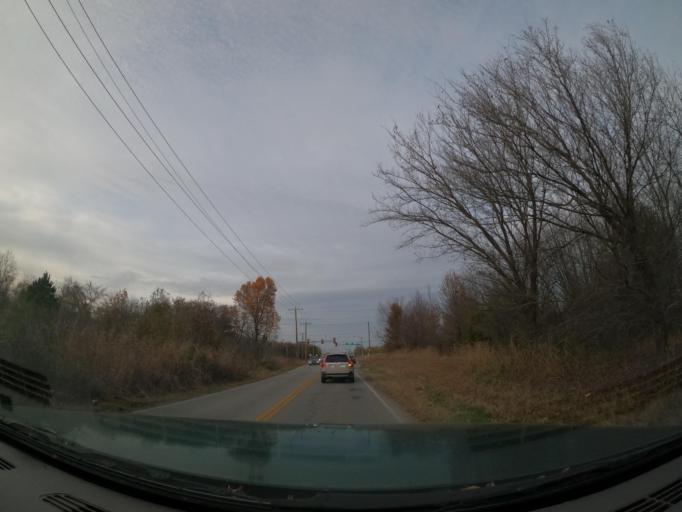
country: US
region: Oklahoma
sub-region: Tulsa County
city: Broken Arrow
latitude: 35.9874
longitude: -95.8153
